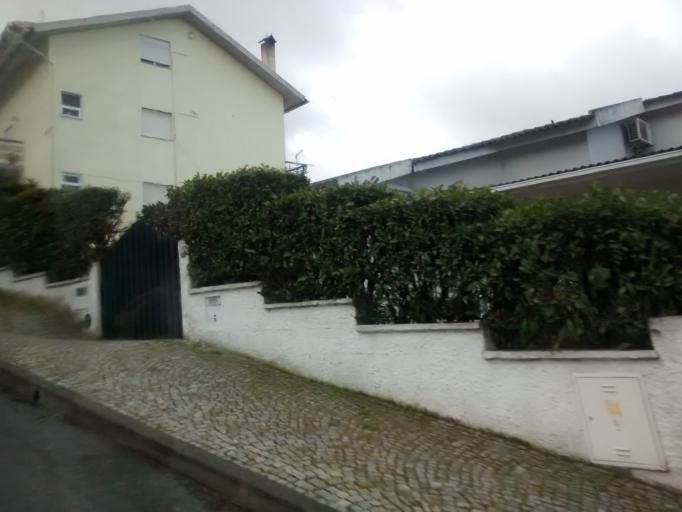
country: PT
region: Guarda
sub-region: Seia
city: Seia
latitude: 40.4136
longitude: -7.7041
